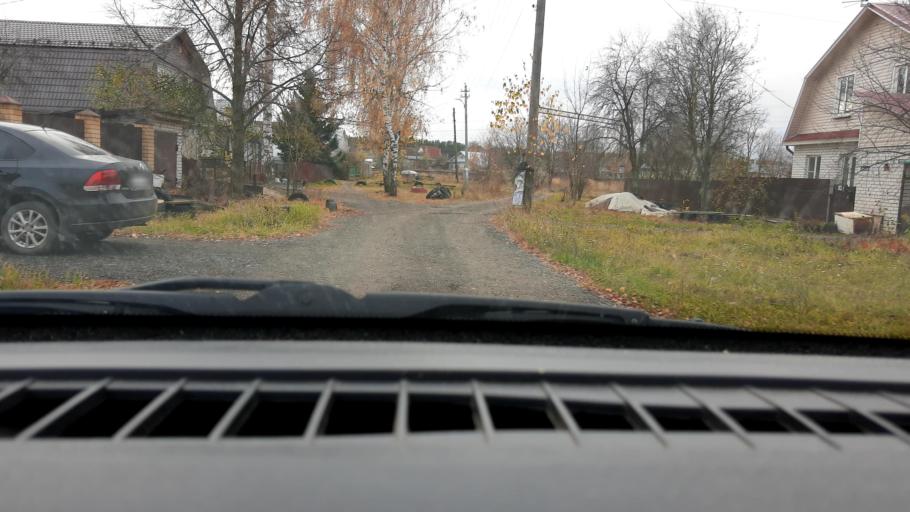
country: RU
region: Nizjnij Novgorod
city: Lukino
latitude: 56.4026
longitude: 43.7200
